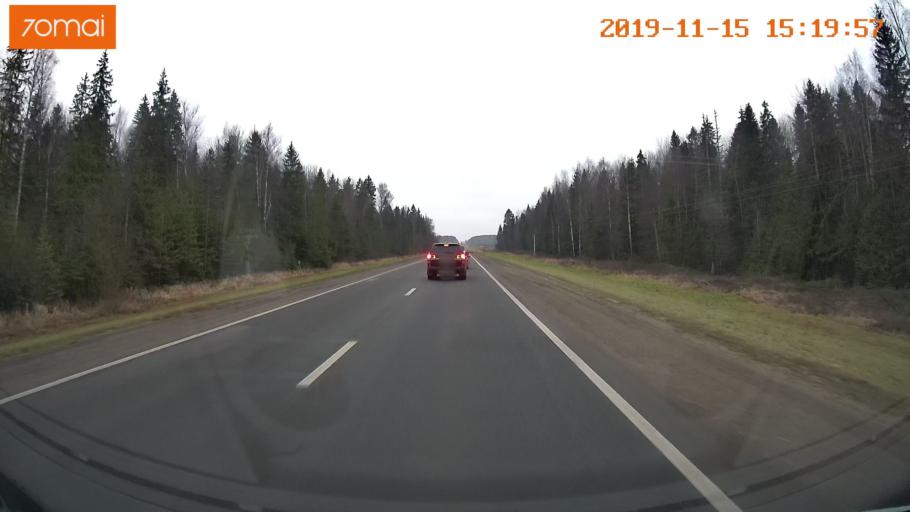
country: RU
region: Jaroslavl
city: Danilov
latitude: 58.2290
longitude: 40.1698
